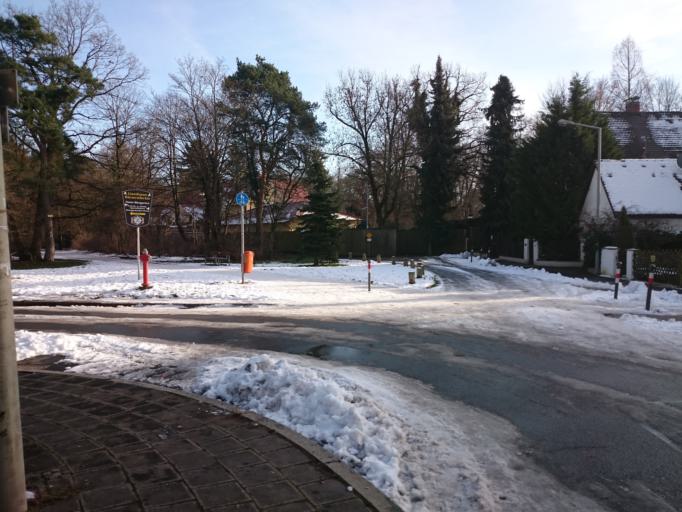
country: DE
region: Bavaria
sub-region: Regierungsbezirk Mittelfranken
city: Nuernberg
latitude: 49.4405
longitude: 11.1285
